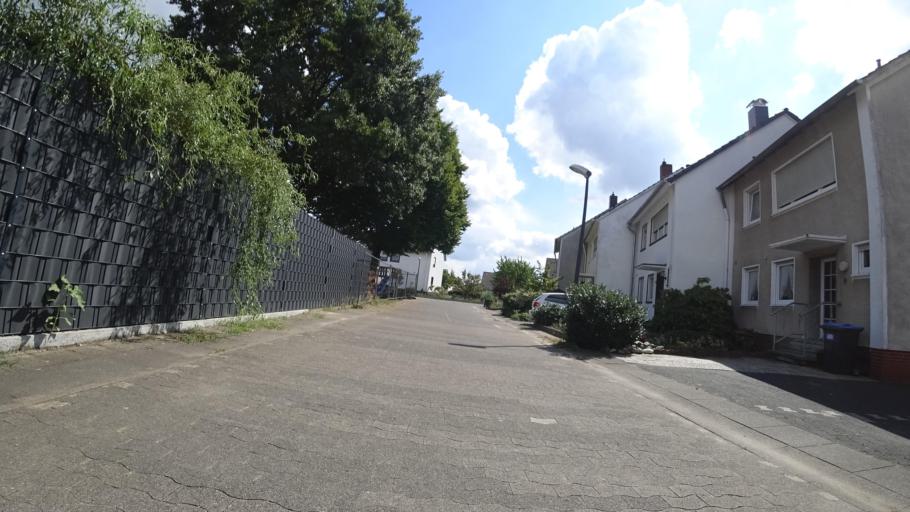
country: DE
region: North Rhine-Westphalia
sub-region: Regierungsbezirk Detmold
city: Guetersloh
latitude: 51.8765
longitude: 8.4330
